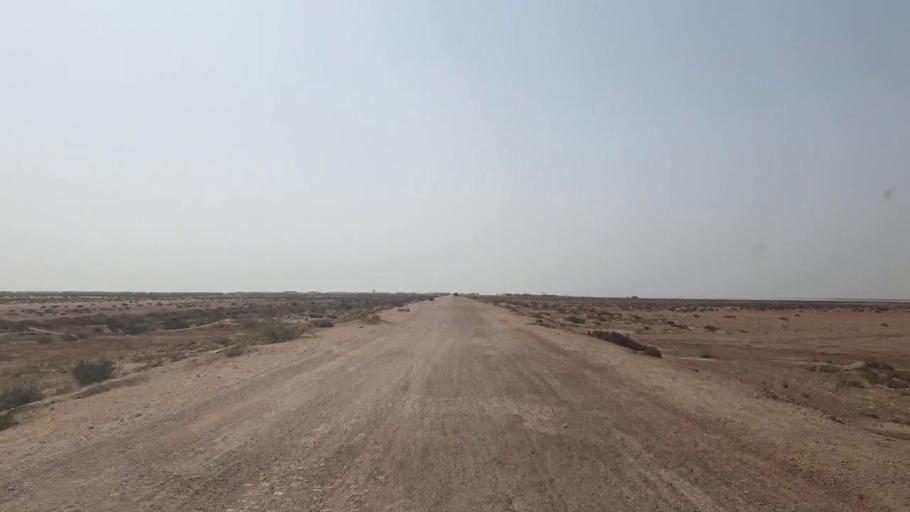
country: PK
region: Sindh
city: Jati
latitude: 24.3512
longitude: 68.5937
